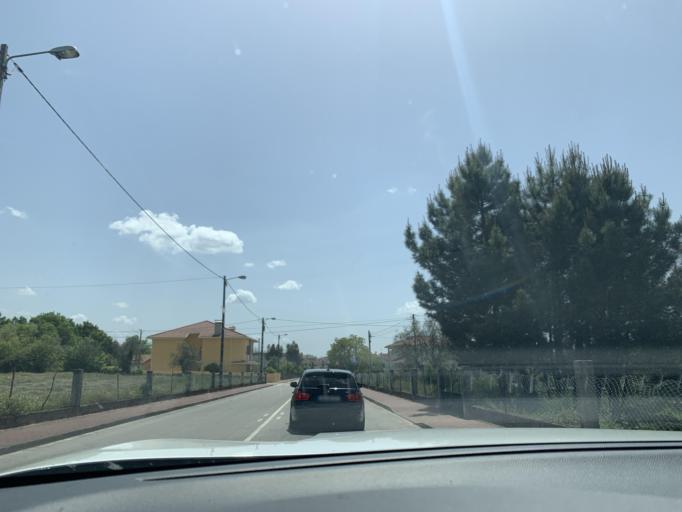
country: PT
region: Viseu
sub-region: Mangualde
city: Mangualde
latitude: 40.6084
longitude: -7.7472
